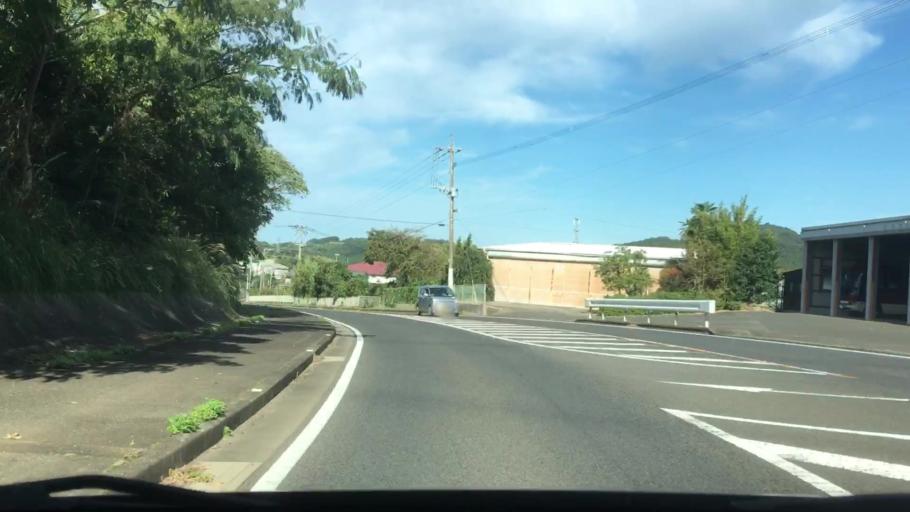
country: JP
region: Nagasaki
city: Sasebo
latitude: 33.0759
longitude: 129.7593
